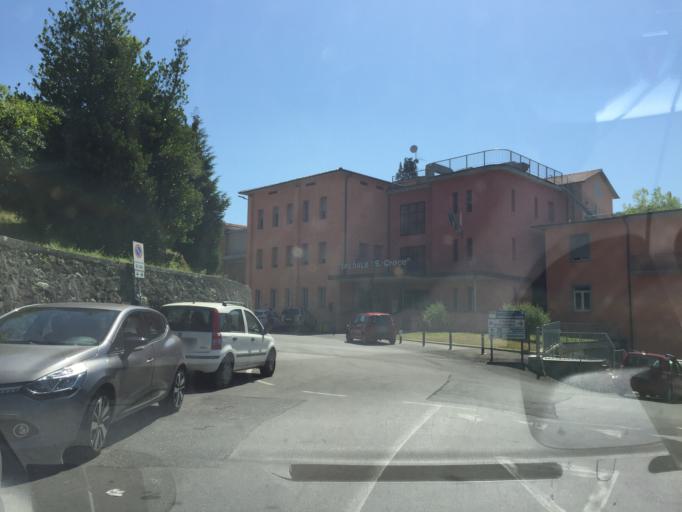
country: IT
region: Tuscany
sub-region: Provincia di Lucca
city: Castelnuovo di Garfagnana
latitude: 44.1127
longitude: 10.4135
